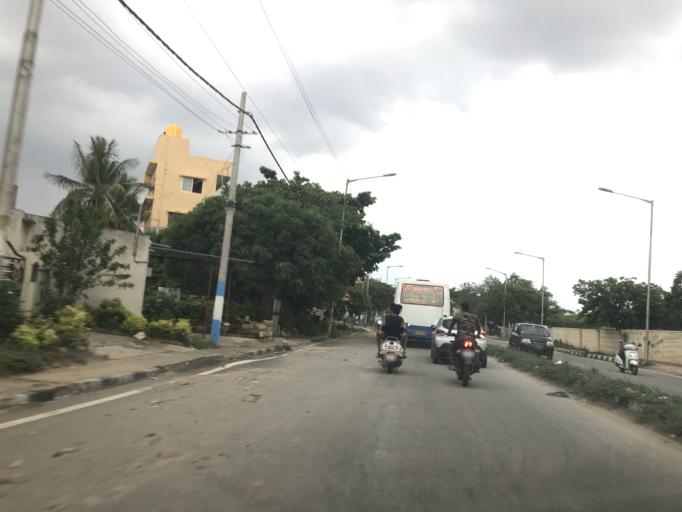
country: IN
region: Karnataka
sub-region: Bangalore Urban
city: Yelahanka
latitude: 13.1281
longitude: 77.6467
